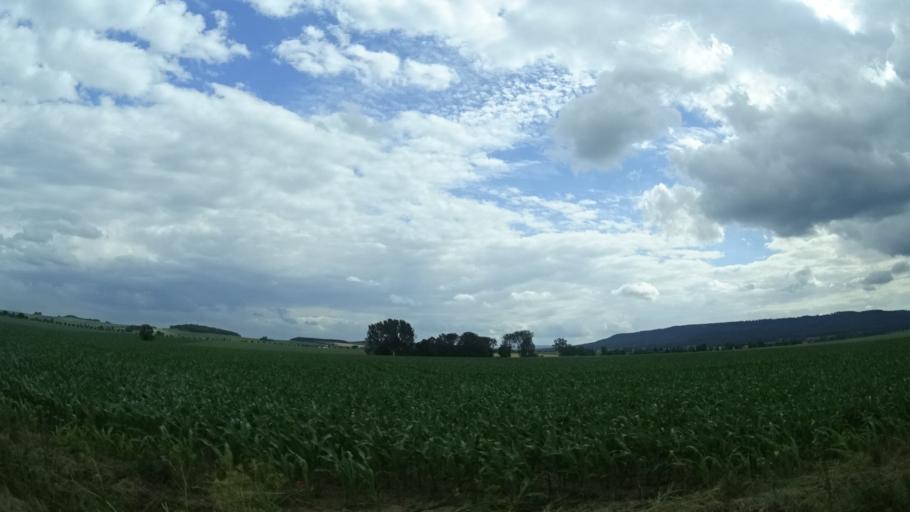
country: DE
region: Lower Saxony
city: Elze
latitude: 52.1704
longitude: 9.6883
